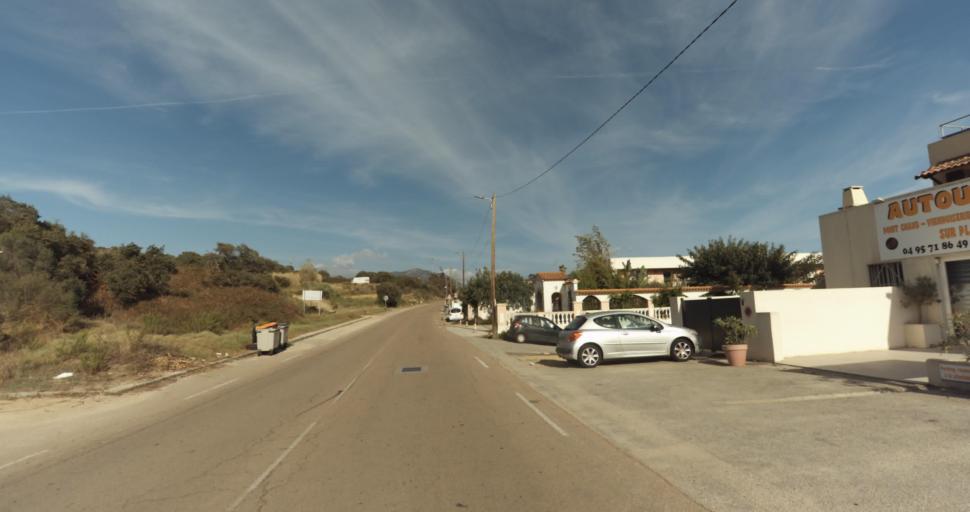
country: FR
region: Corsica
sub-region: Departement de la Corse-du-Sud
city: Ajaccio
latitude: 41.9292
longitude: 8.7715
